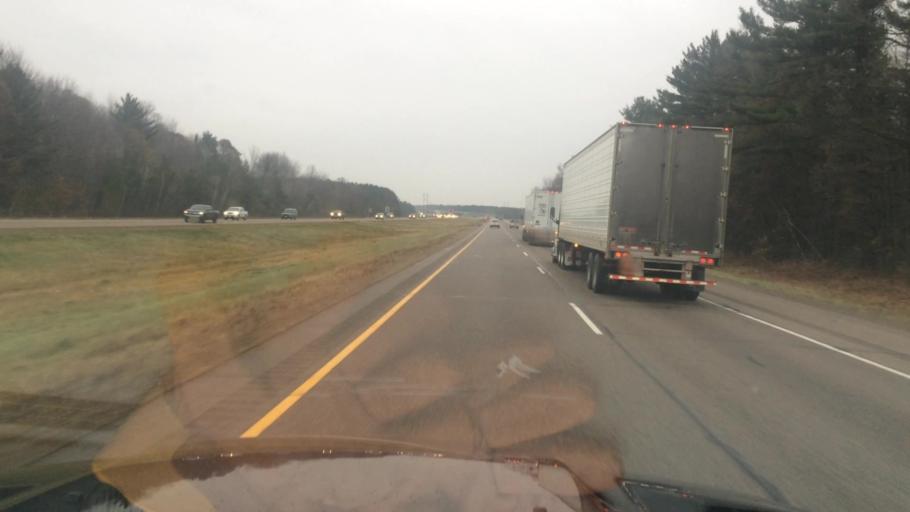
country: US
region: Wisconsin
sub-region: Portage County
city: Stevens Point
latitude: 44.5812
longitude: -89.6060
